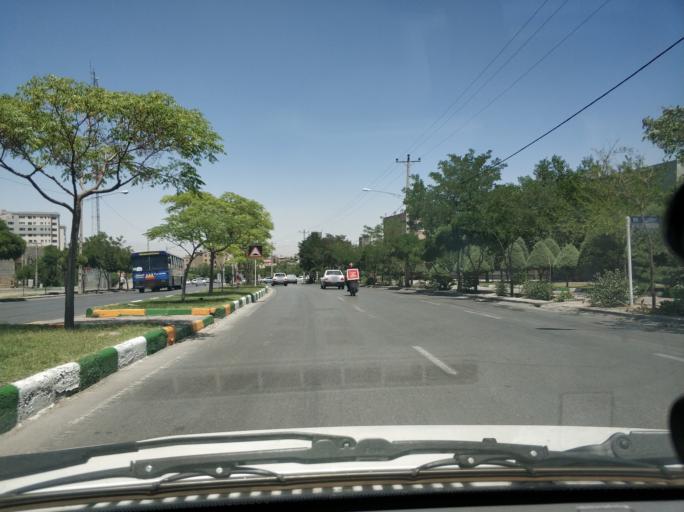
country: IR
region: Razavi Khorasan
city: Mashhad
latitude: 36.2966
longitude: 59.5077
